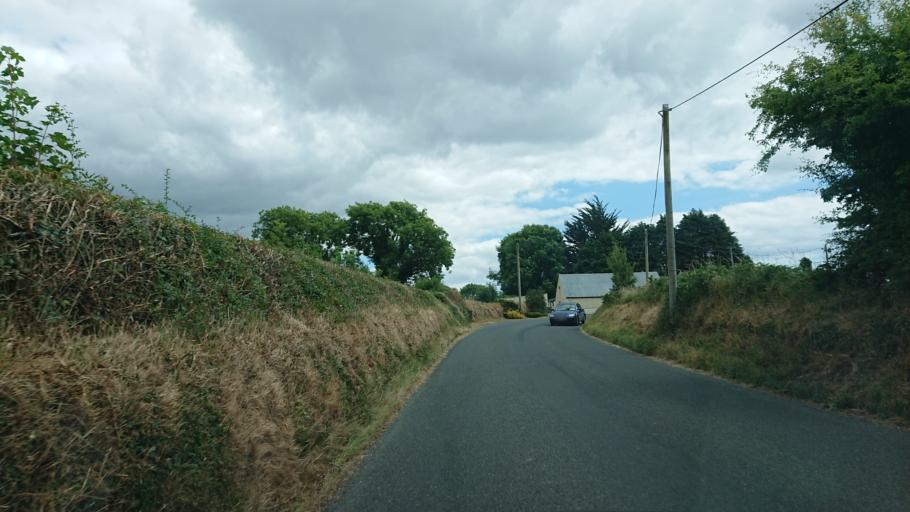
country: IE
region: Munster
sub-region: Waterford
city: Portlaw
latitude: 52.2250
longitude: -7.3375
